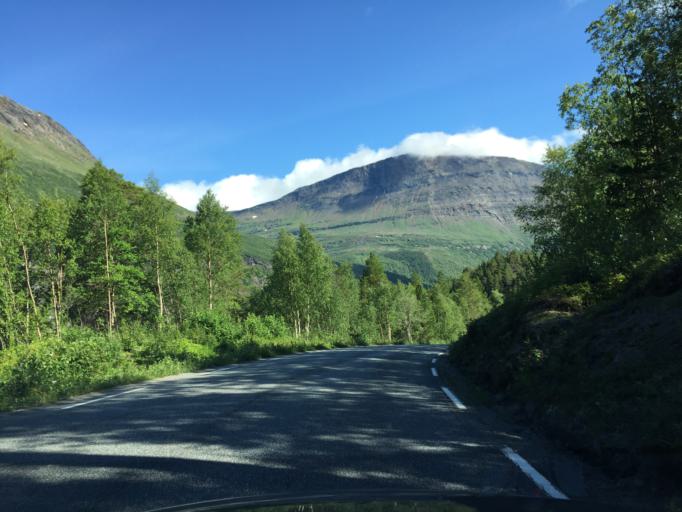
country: NO
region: Nordland
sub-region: Saltdal
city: Rognan
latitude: 66.8176
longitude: 15.4636
